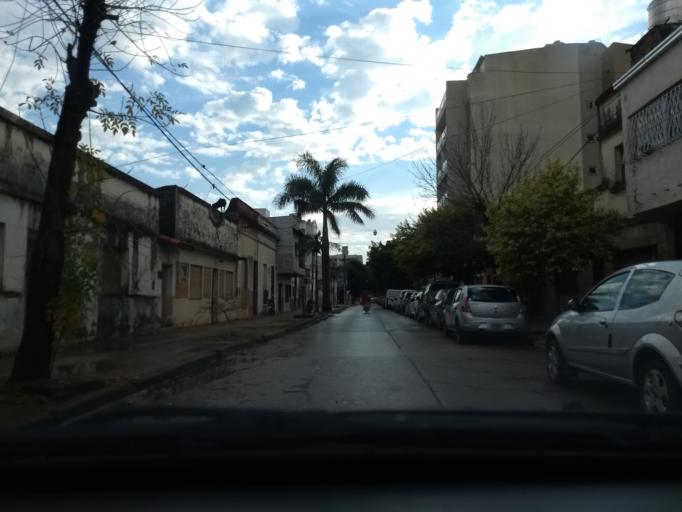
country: AR
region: Corrientes
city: Corrientes
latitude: -27.4728
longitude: -58.8284
